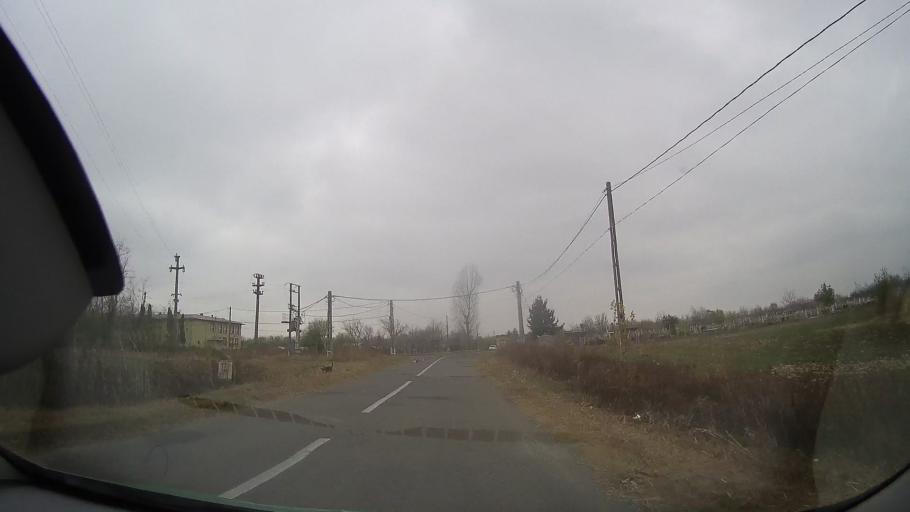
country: RO
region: Ialomita
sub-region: Comuna Valea Macrisului
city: Valea Macrisului
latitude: 44.7401
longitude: 26.8391
